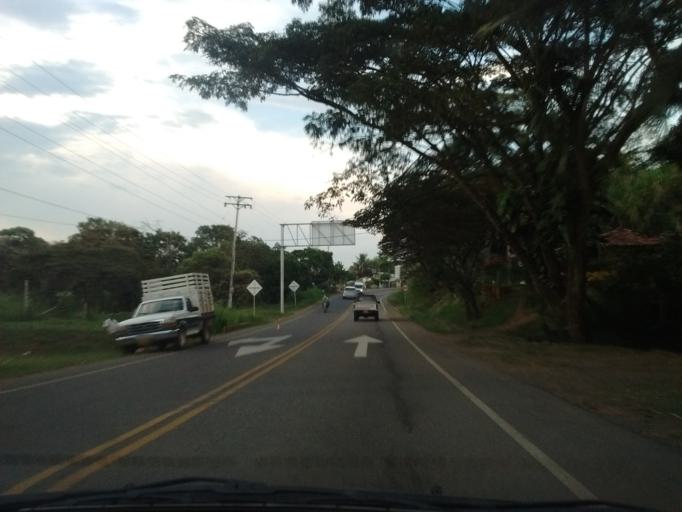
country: CO
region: Cauca
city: Santander de Quilichao
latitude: 2.9957
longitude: -76.4941
